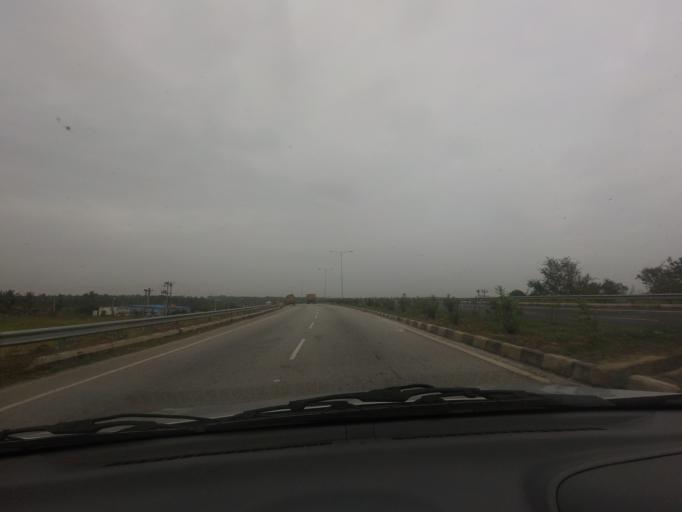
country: IN
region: Karnataka
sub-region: Tumkur
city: Kunigal
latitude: 13.0032
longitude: 76.9559
